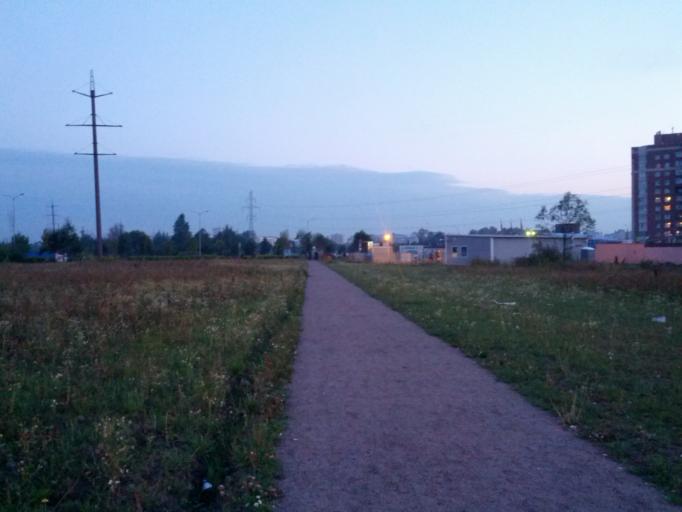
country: RU
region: St.-Petersburg
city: Krasnogvargeisky
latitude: 59.9124
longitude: 30.5032
